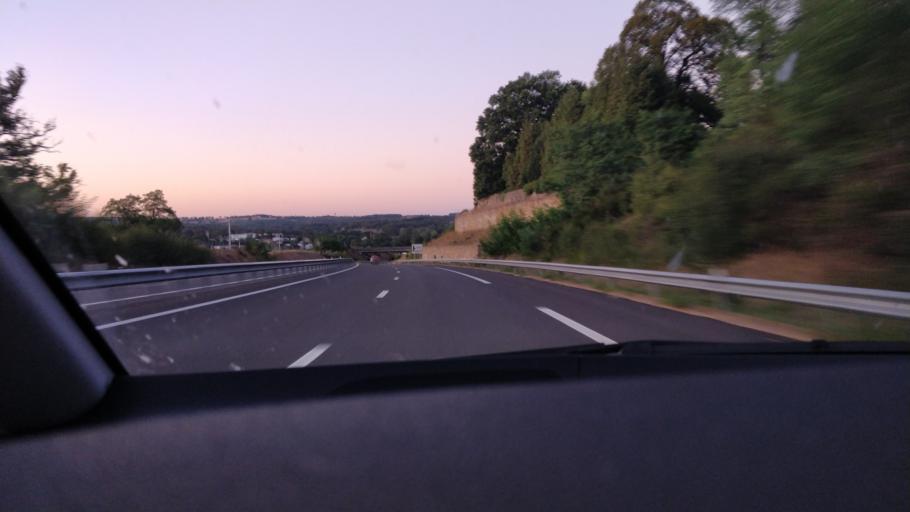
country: FR
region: Poitou-Charentes
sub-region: Departement de la Charente
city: Chabanais
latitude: 45.8680
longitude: 0.7369
